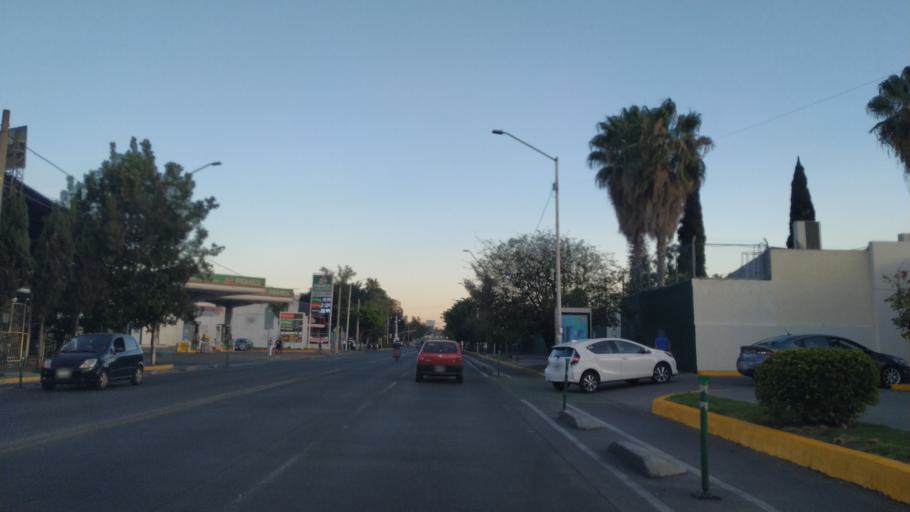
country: MX
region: Jalisco
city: Tlaquepaque
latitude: 20.6518
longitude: -103.3248
